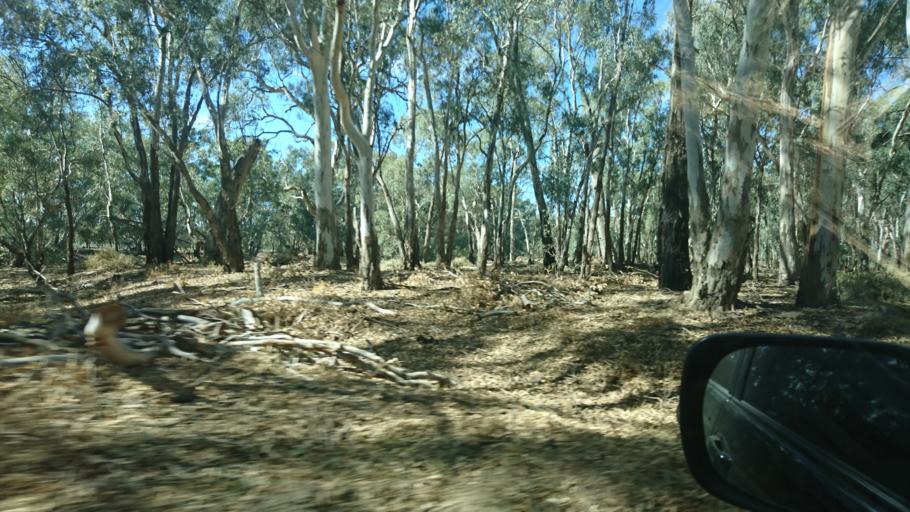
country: AU
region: Victoria
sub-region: Swan Hill
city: Swan Hill
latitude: -35.1409
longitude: 143.3860
